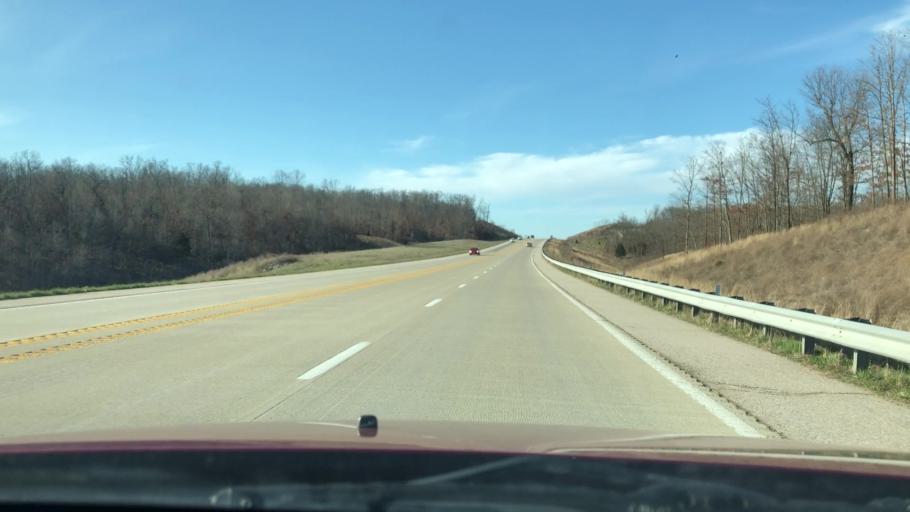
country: US
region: Missouri
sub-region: Camden County
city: Camdenton
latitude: 37.9298
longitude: -92.7136
